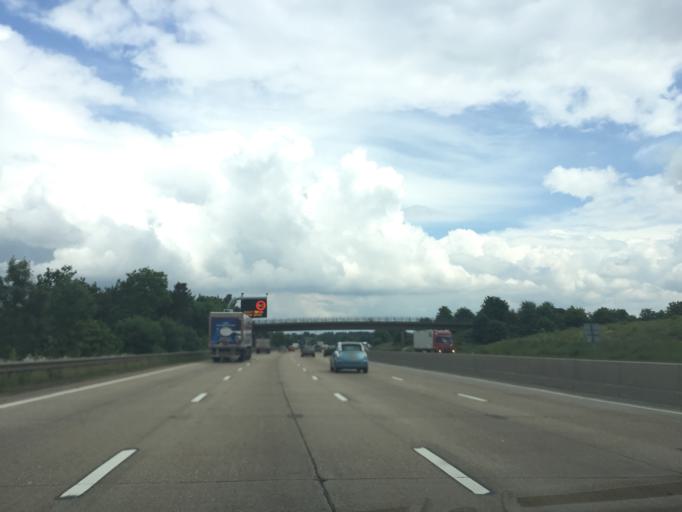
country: GB
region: England
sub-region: Hertfordshire
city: Cuffley
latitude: 51.6882
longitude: -0.1366
